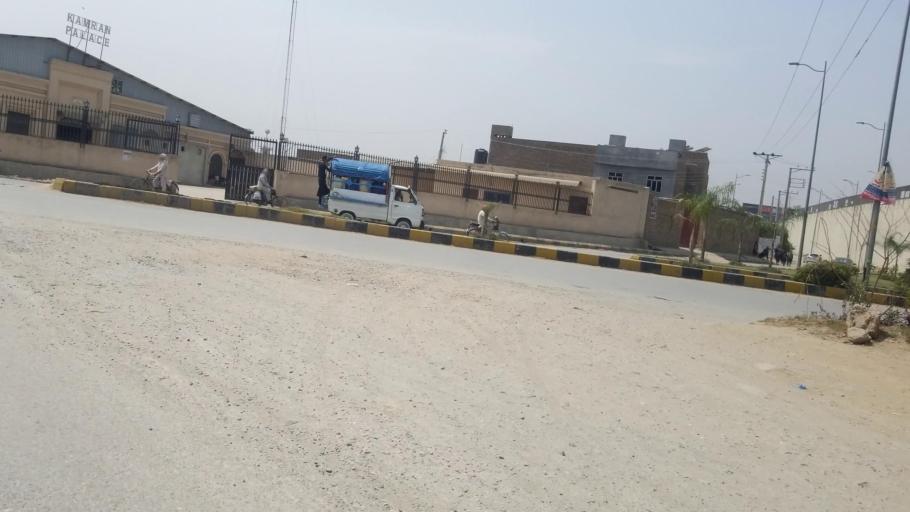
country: PK
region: Khyber Pakhtunkhwa
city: Peshawar
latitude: 34.0311
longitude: 71.5549
